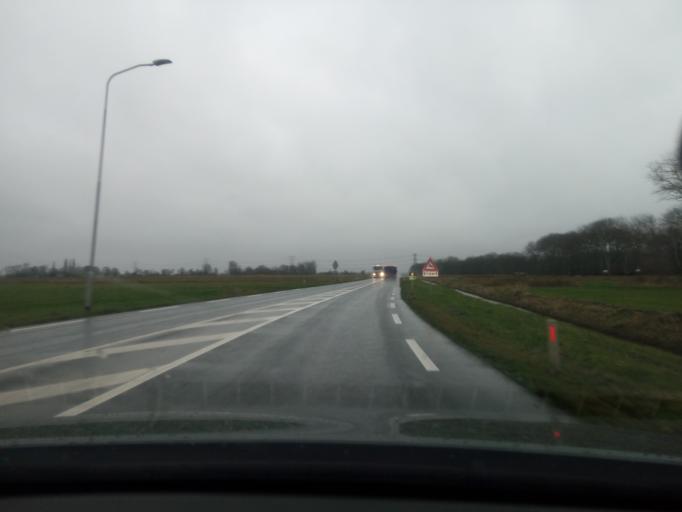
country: NL
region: Groningen
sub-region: Gemeente Appingedam
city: Appingedam
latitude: 53.3186
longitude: 6.7960
